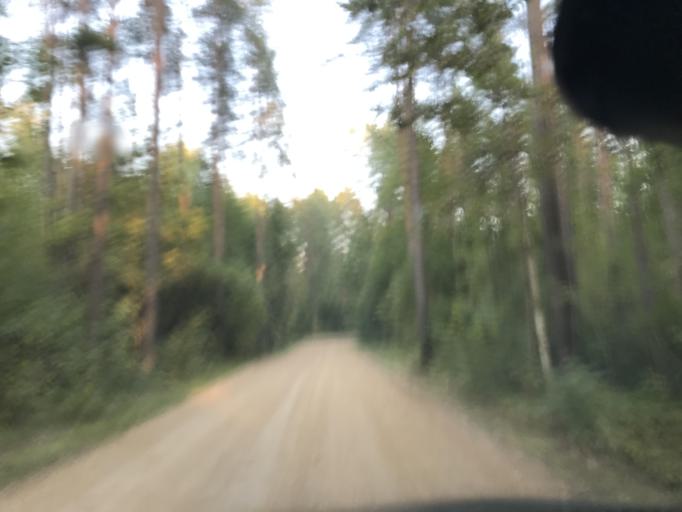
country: LV
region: Ikskile
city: Ikskile
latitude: 56.8311
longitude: 24.5082
